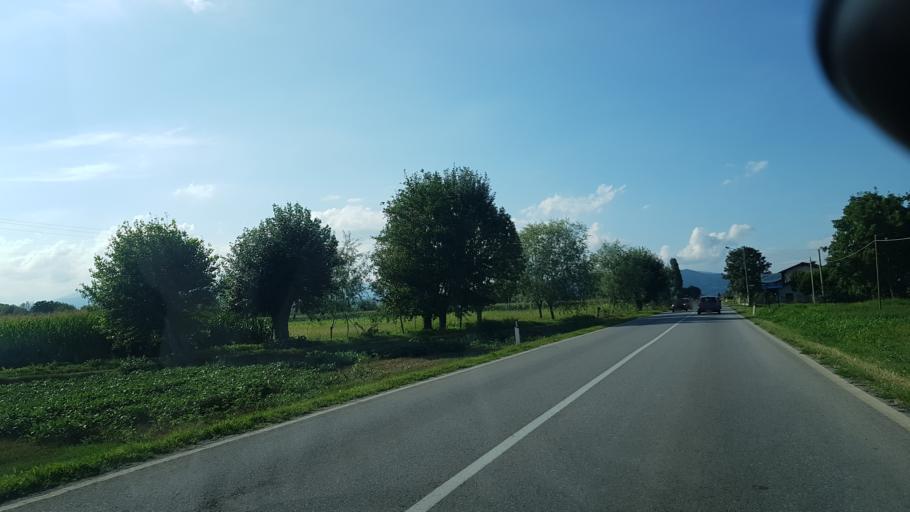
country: IT
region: Piedmont
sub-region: Provincia di Cuneo
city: Roata Rossi
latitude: 44.4634
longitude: 7.5167
